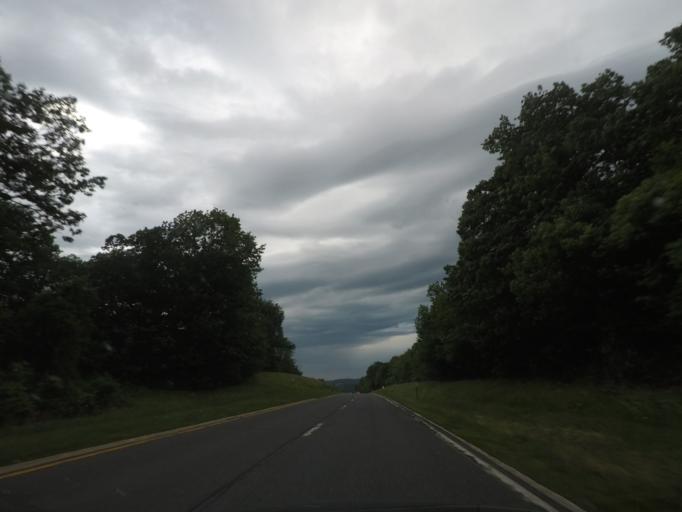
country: US
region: New York
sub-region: Dutchess County
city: Pine Plains
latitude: 42.1010
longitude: -73.7179
